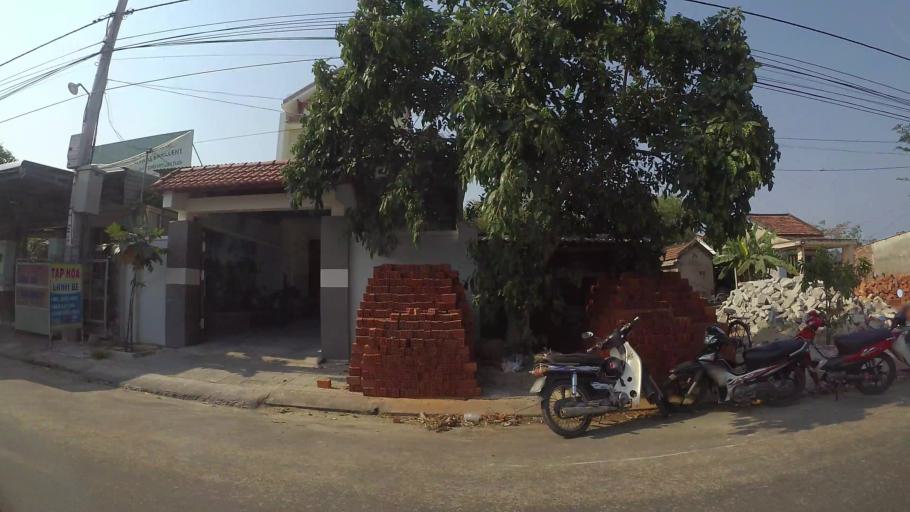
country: VN
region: Da Nang
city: Ngu Hanh Son
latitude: 15.9535
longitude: 108.2779
